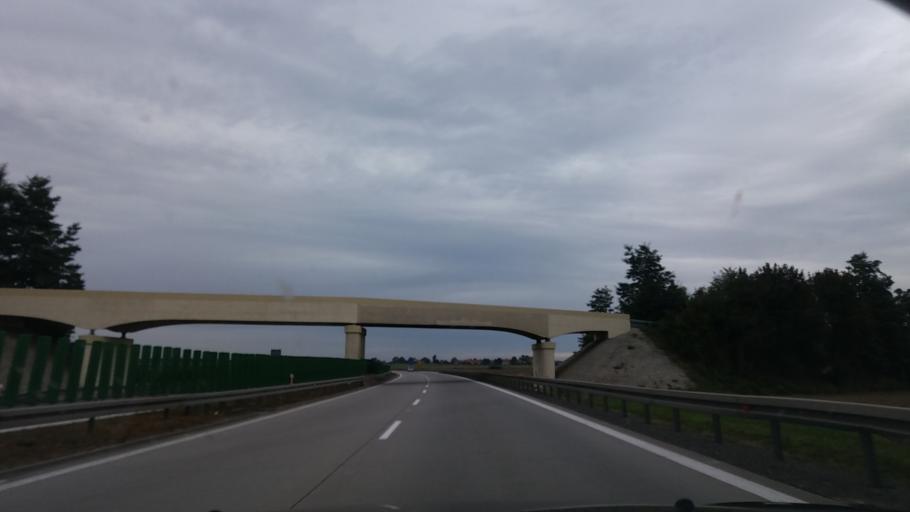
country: PL
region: Lower Silesian Voivodeship
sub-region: Powiat sredzki
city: Udanin
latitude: 51.1065
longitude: 16.3996
